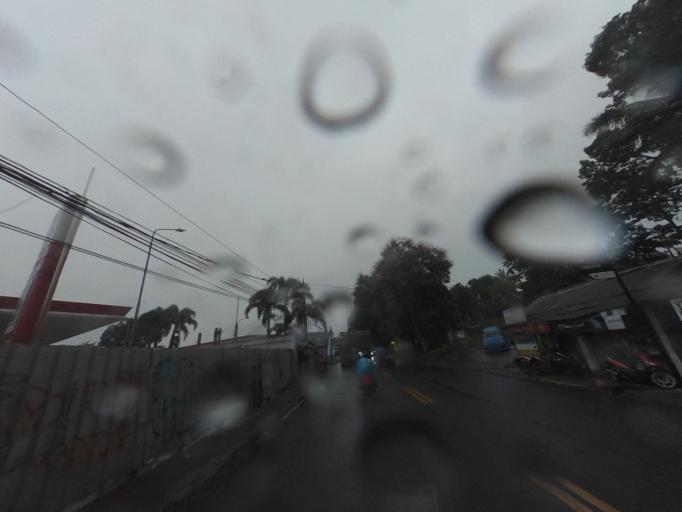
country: ID
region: West Java
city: Caringin
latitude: -6.6589
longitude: 106.8575
